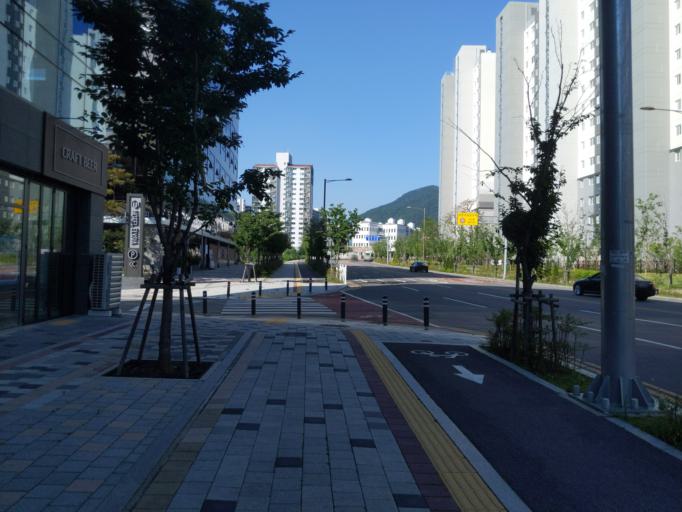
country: KR
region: Daegu
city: Hwawon
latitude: 35.8006
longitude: 128.5331
